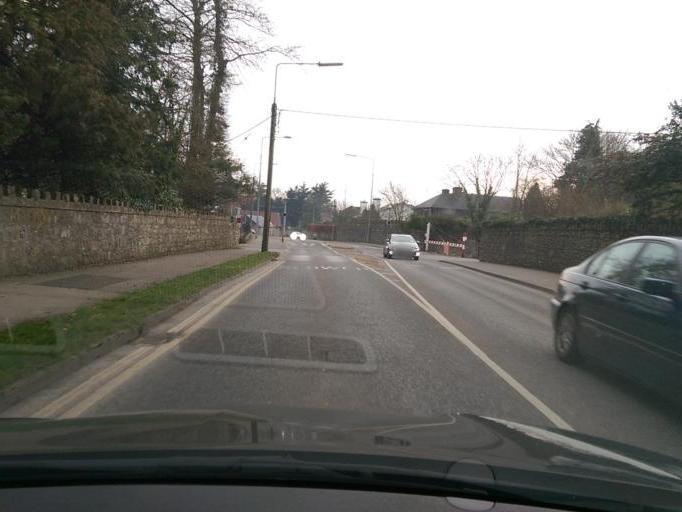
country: IE
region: Leinster
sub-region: An Iarmhi
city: Athlone
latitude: 53.4284
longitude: -7.9312
